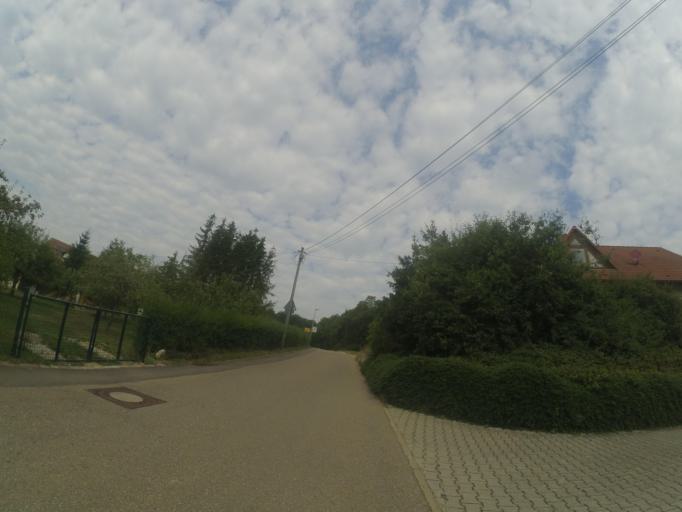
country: DE
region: Baden-Wuerttemberg
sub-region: Tuebingen Region
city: Westerstetten
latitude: 48.5076
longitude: 9.9232
